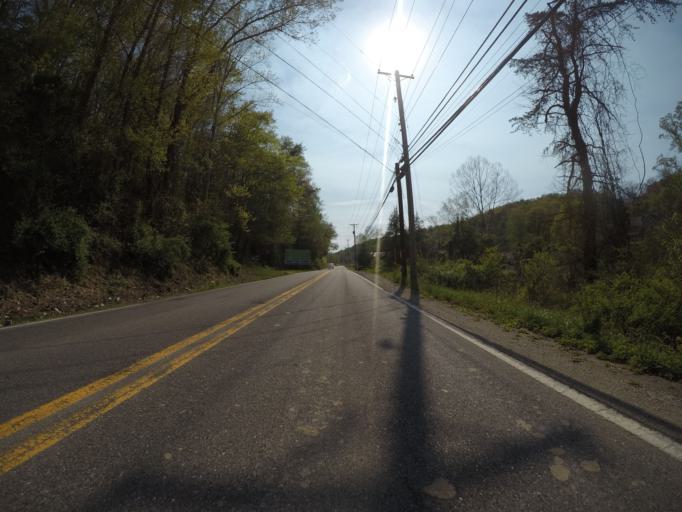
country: US
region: West Virginia
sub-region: Kanawha County
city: Charleston
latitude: 38.3761
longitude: -81.5682
